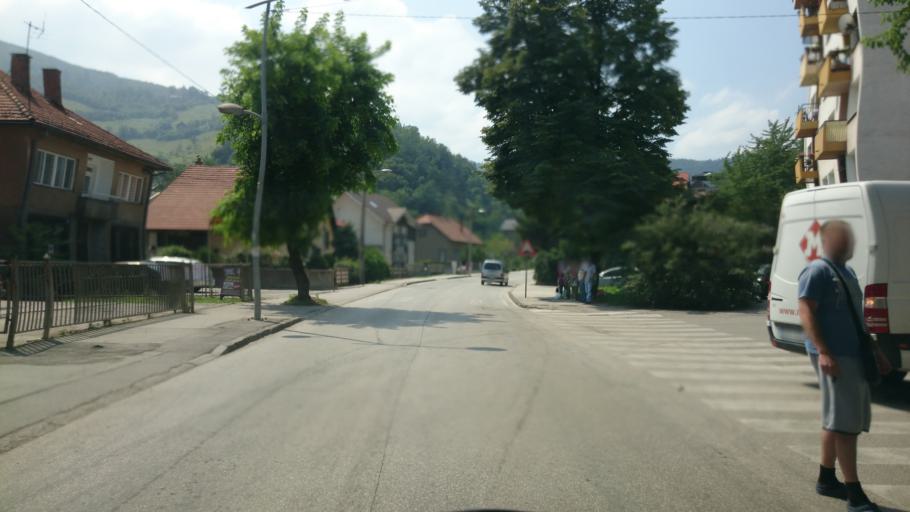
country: BA
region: Federation of Bosnia and Herzegovina
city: Zenica
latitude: 44.1979
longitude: 17.8972
